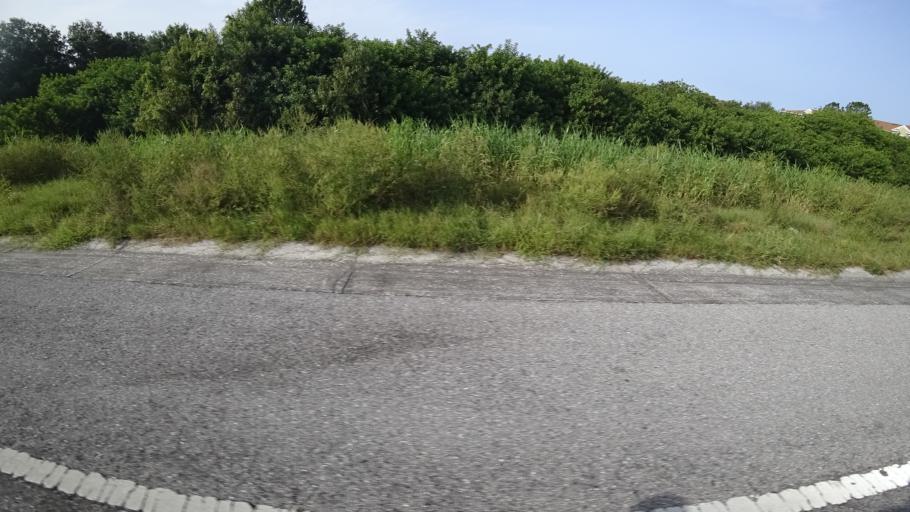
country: US
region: Florida
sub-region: Manatee County
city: Ellenton
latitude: 27.5468
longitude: -82.5083
